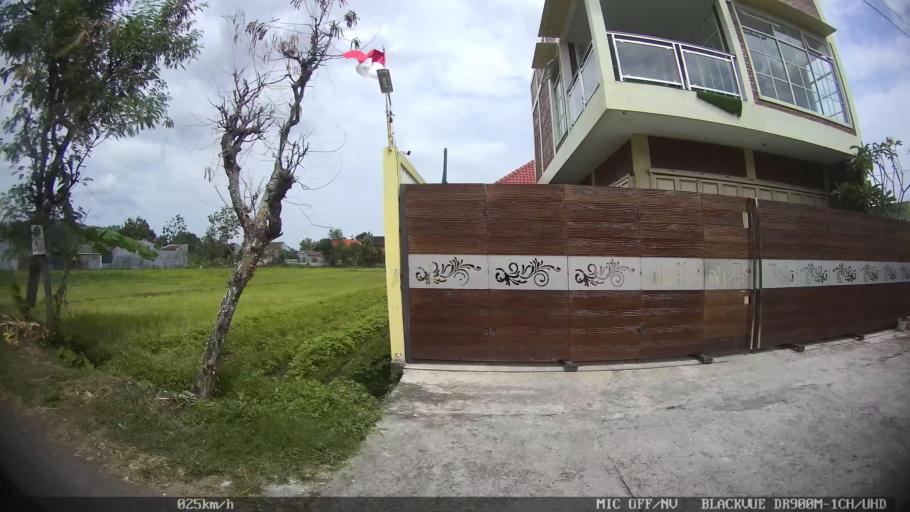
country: ID
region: Daerah Istimewa Yogyakarta
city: Depok
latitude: -7.8301
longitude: 110.4632
